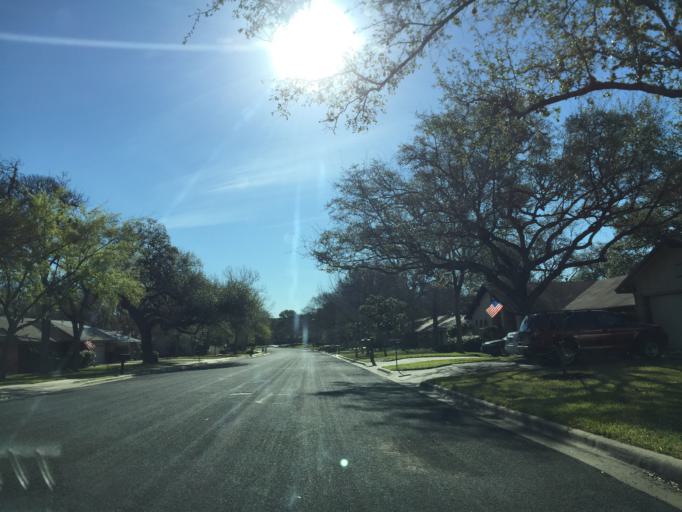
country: US
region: Texas
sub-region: Williamson County
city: Jollyville
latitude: 30.4021
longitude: -97.7337
